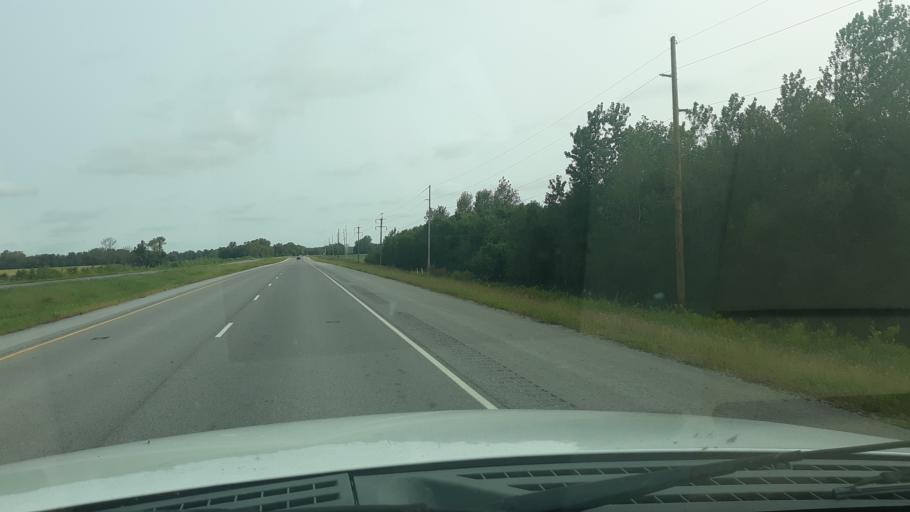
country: US
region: Illinois
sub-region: Saline County
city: Eldorado
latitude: 37.8679
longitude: -88.3991
